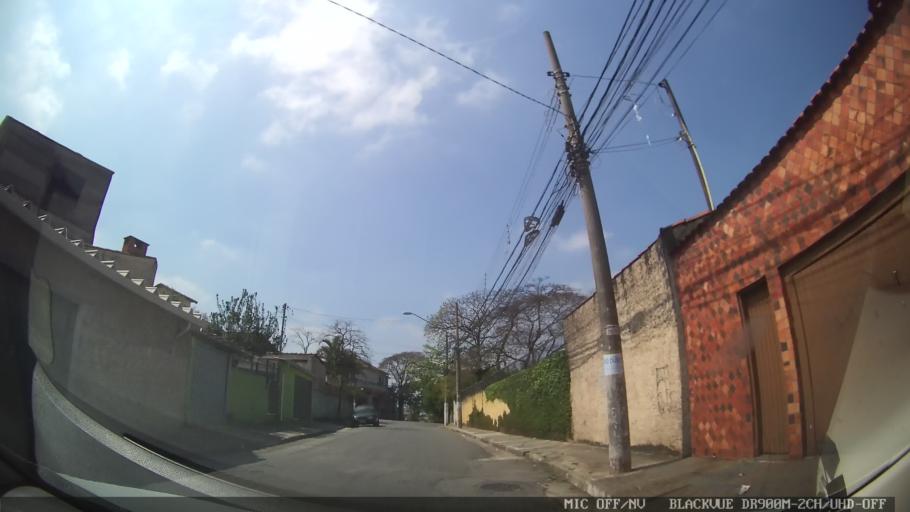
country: BR
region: Sao Paulo
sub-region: Sao Paulo
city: Sao Paulo
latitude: -23.5005
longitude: -46.6676
